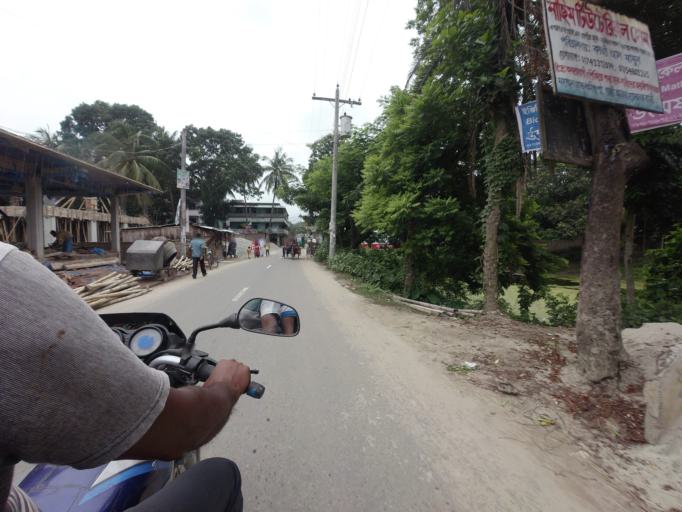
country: BD
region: Khulna
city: Kalia
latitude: 23.1794
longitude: 89.6477
